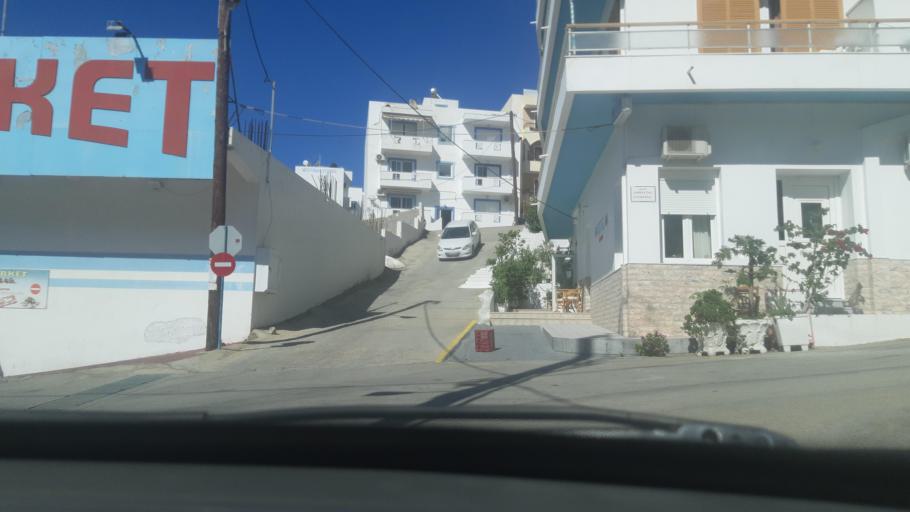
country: GR
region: South Aegean
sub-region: Nomos Dodekanisou
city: Karpathos
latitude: 35.5068
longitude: 27.2155
